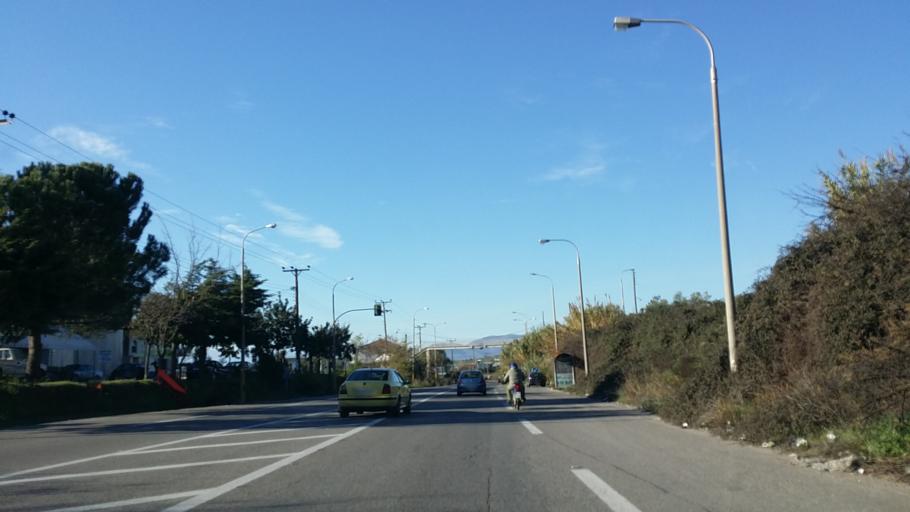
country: GR
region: West Greece
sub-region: Nomos Aitolias kai Akarnanias
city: Megali Khora
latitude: 38.6499
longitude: 21.3775
